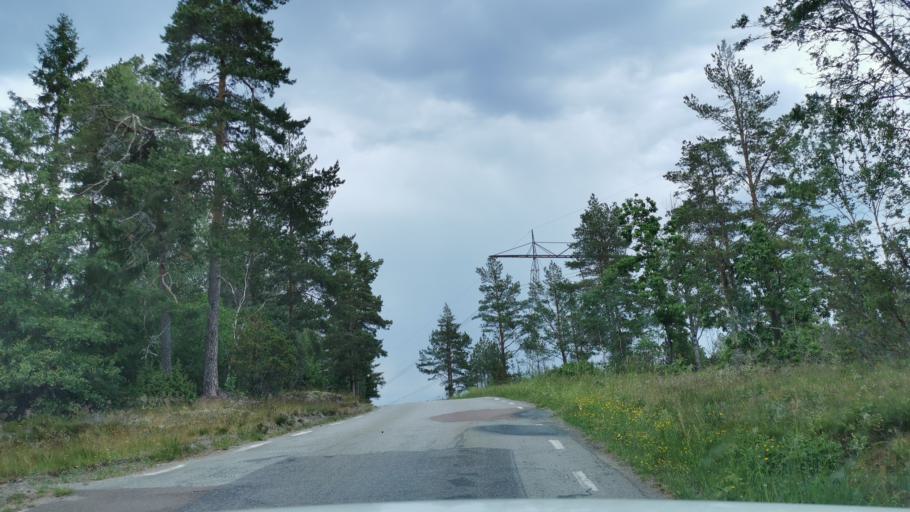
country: SE
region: Vaestra Goetaland
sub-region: Bengtsfors Kommun
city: Dals Langed
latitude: 58.8706
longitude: 12.4030
